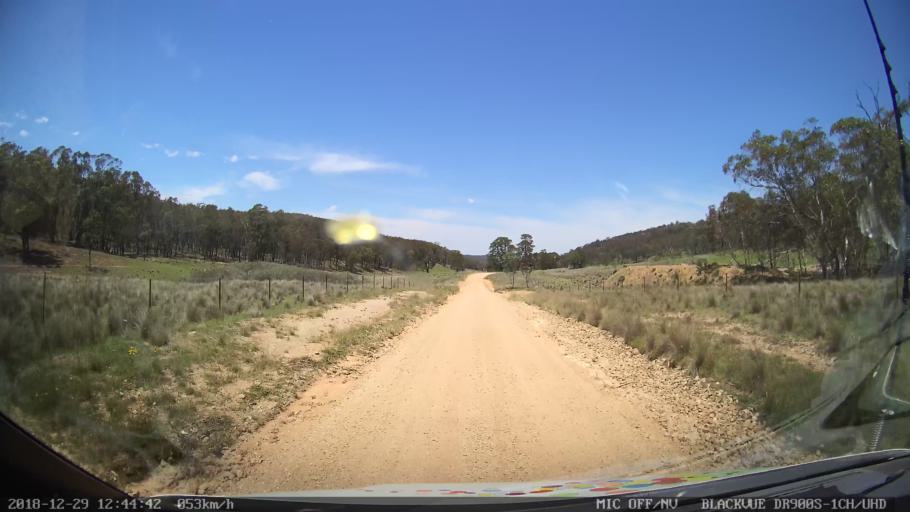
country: AU
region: Australian Capital Territory
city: Macarthur
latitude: -35.6294
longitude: 149.2158
